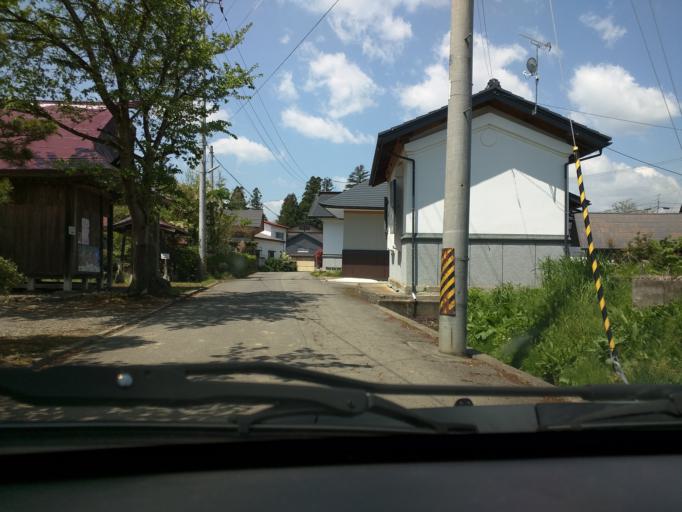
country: JP
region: Fukushima
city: Kitakata
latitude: 37.6085
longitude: 139.8457
